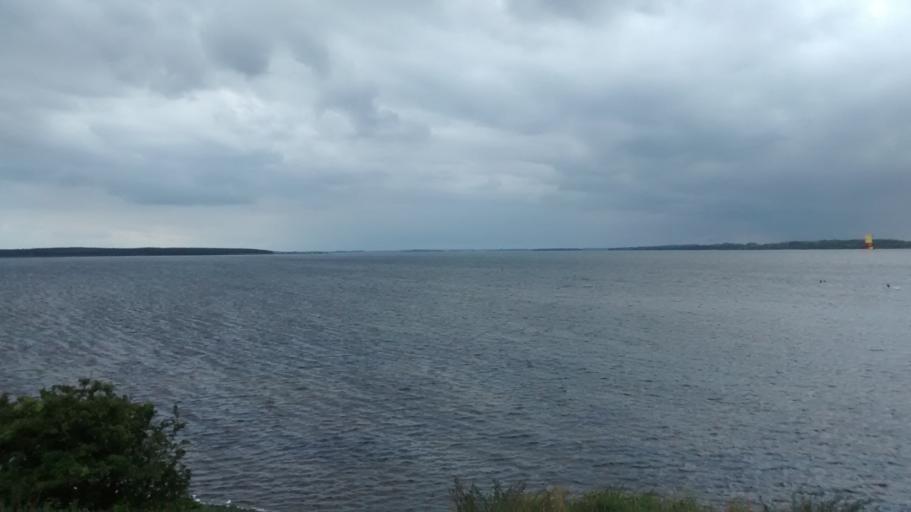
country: DE
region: Mecklenburg-Vorpommern
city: Bastorf
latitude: 54.0954
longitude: 11.6214
